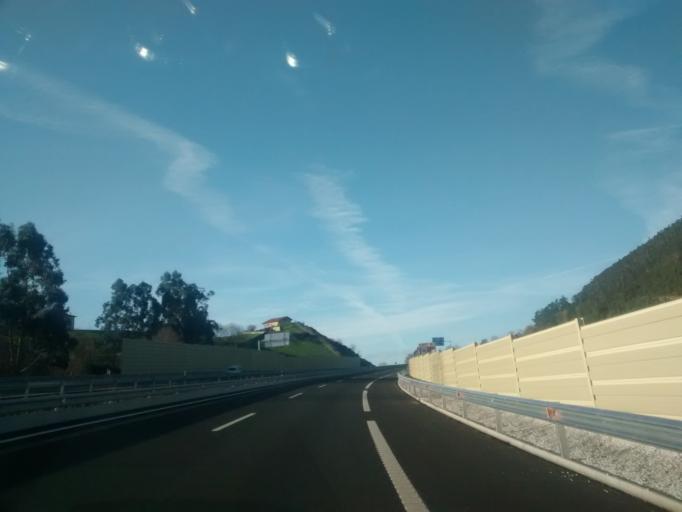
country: ES
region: Cantabria
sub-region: Provincia de Cantabria
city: Lierganes
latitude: 43.3763
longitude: -3.7506
